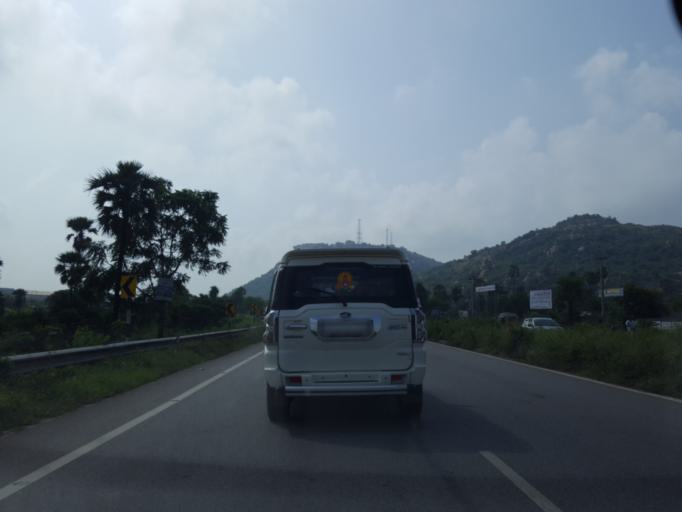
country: IN
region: Telangana
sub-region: Rangareddi
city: Ghatkesar
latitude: 17.2969
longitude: 78.7405
